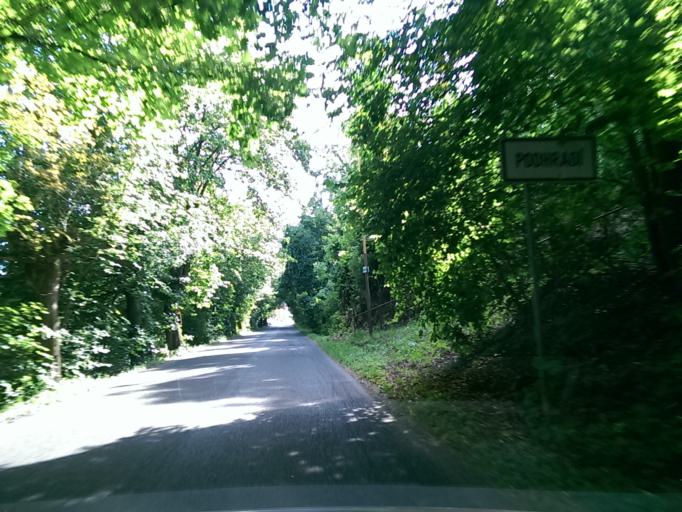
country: CZ
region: Central Bohemia
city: Bakov nad Jizerou
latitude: 50.4718
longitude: 14.9234
